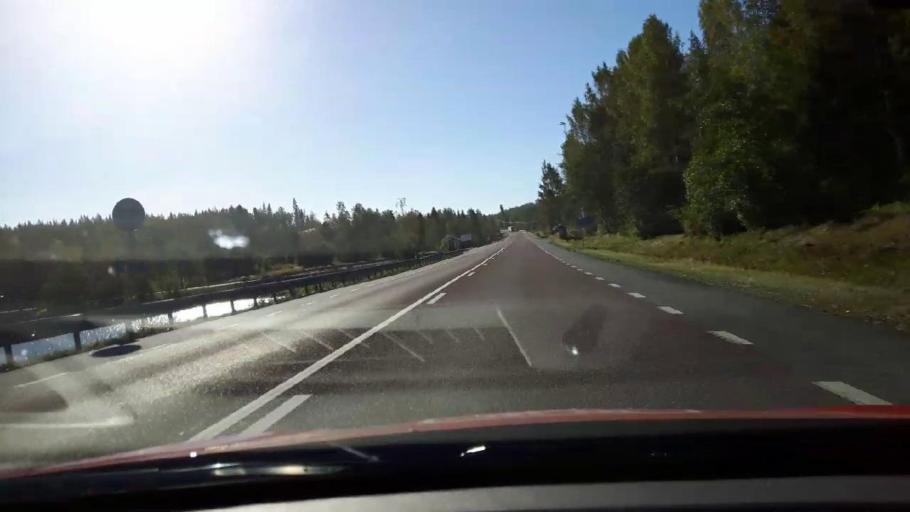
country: SE
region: Jaemtland
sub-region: Braecke Kommun
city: Braecke
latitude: 62.9523
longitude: 15.1600
